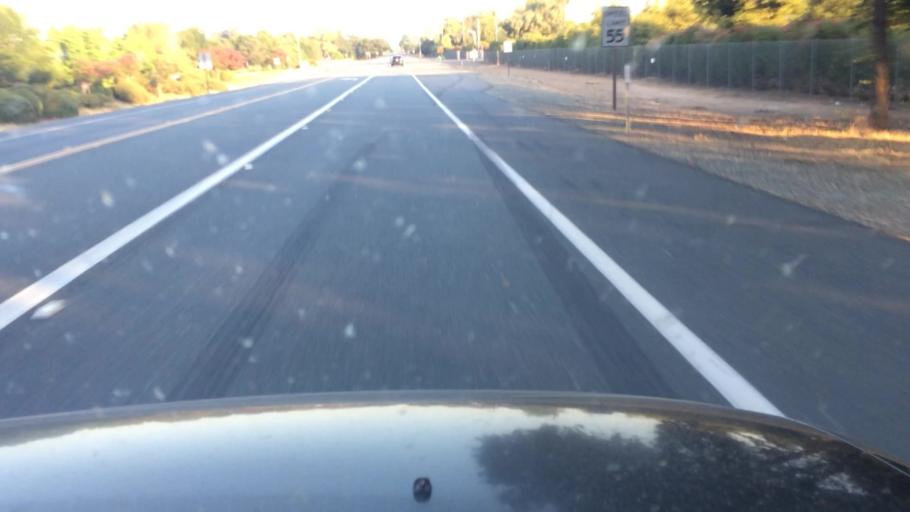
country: US
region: California
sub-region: Amador County
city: Ione
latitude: 38.3643
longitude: -120.9469
